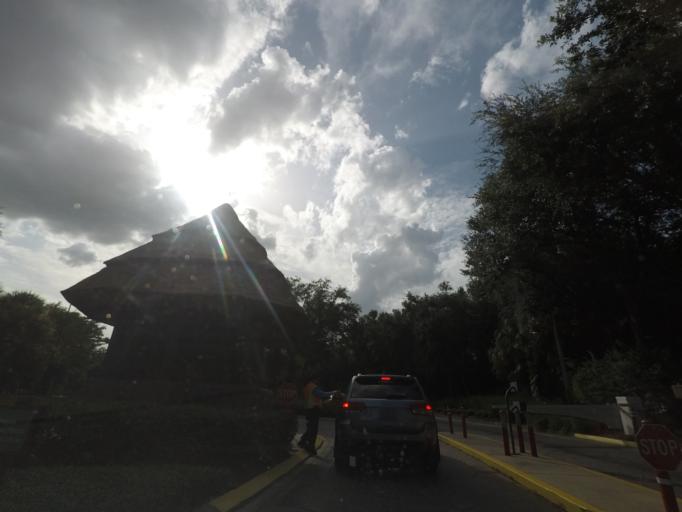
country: US
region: Florida
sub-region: Polk County
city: Citrus Ridge
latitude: 28.3518
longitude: -81.5996
